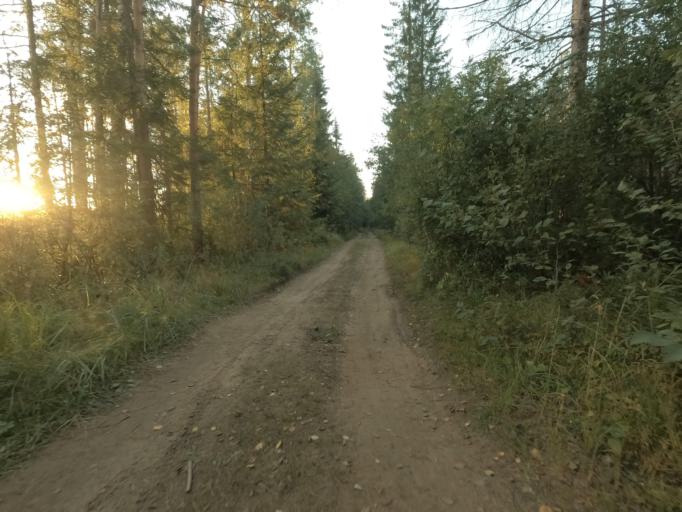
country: RU
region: Leningrad
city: Otradnoye
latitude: 59.8243
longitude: 30.8214
